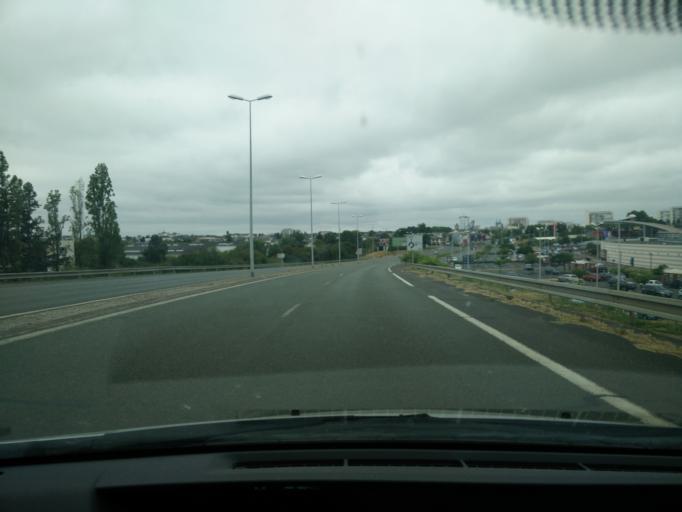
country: FR
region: Pays de la Loire
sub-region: Departement de Maine-et-Loire
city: Angers
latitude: 47.4659
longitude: -0.5200
